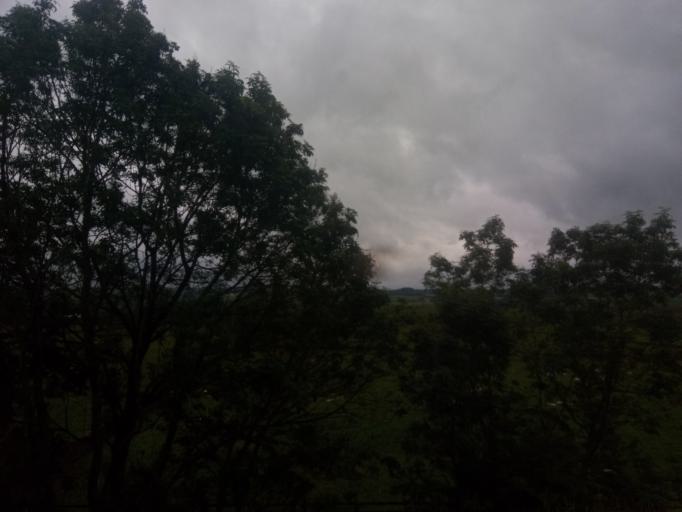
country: GB
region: England
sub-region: North Yorkshire
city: Settle
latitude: 54.0237
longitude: -2.2658
